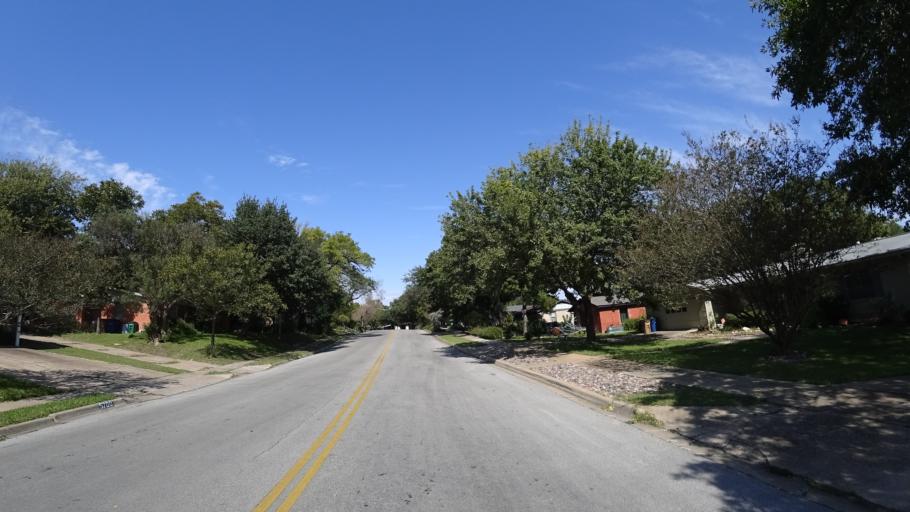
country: US
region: Texas
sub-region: Travis County
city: West Lake Hills
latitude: 30.3353
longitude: -97.7524
